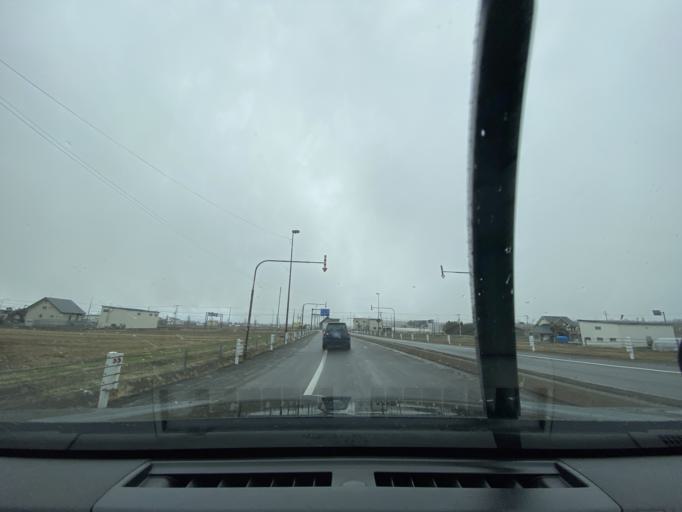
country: JP
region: Hokkaido
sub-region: Asahikawa-shi
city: Asahikawa
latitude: 43.8350
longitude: 142.4068
